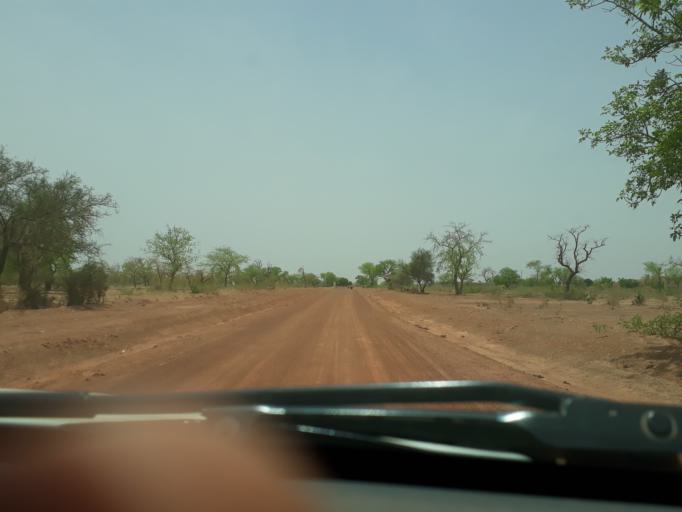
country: BF
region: Plateau-Central
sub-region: Province d'Oubritenga
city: Ziniare
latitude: 12.5796
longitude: -1.3346
